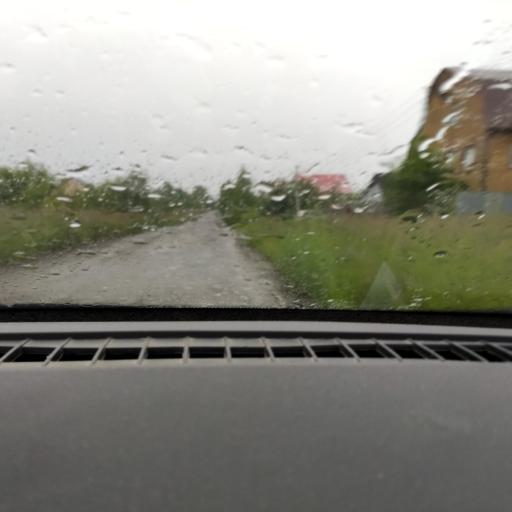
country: RU
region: Perm
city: Perm
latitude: 58.0385
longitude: 56.3722
